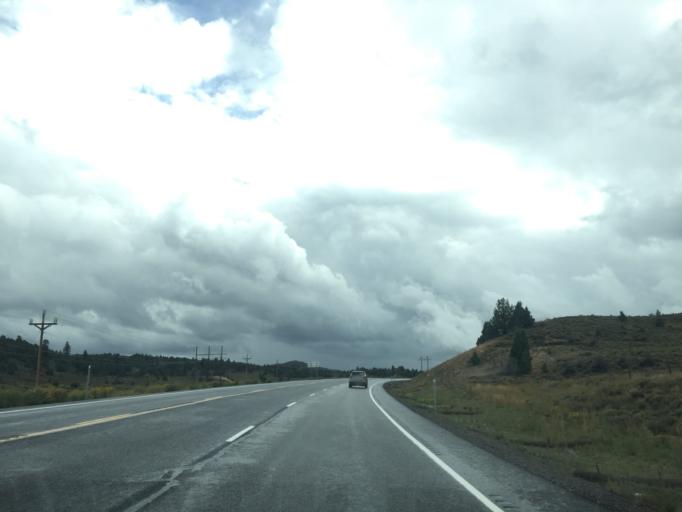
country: US
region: Utah
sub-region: Garfield County
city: Panguitch
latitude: 37.5102
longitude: -112.4976
